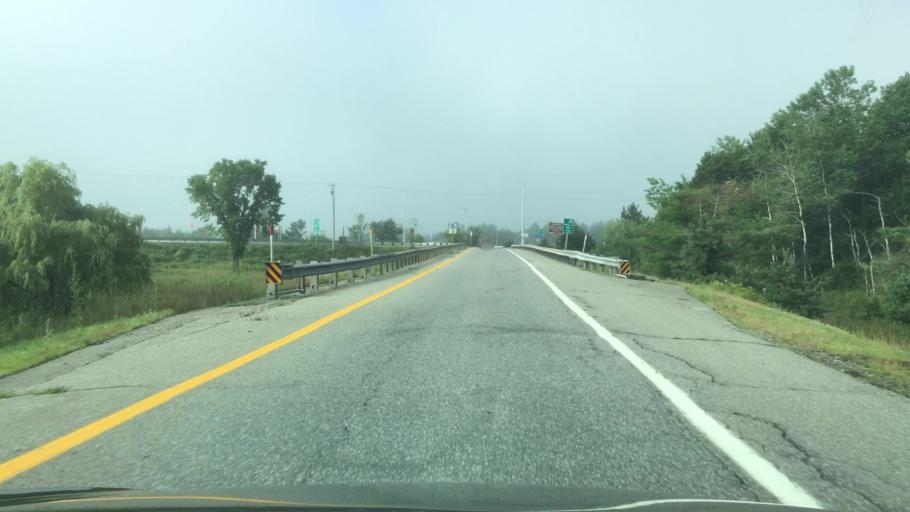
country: US
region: Maine
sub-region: Kennebec County
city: Gardiner
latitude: 44.2105
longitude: -69.8254
